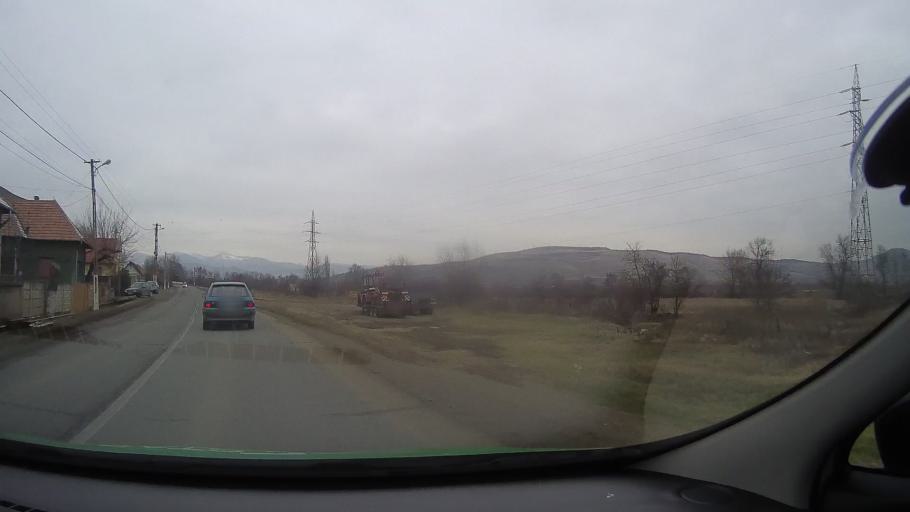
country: RO
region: Alba
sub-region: Comuna Ighiu
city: Sard
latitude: 46.1186
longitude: 23.5363
